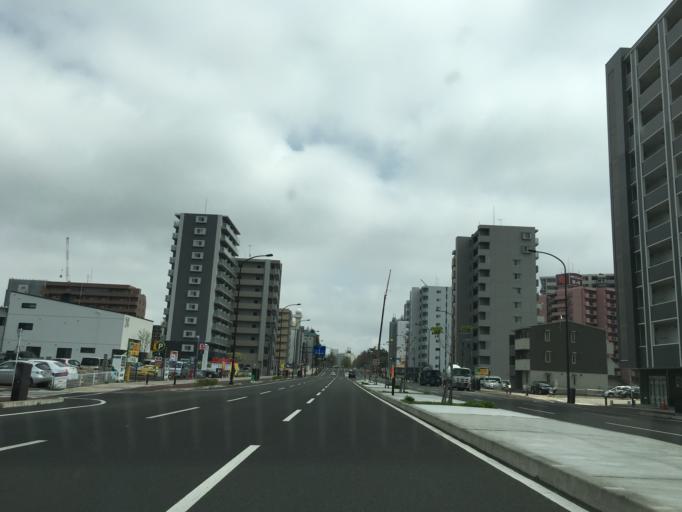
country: JP
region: Miyagi
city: Sendai-shi
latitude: 38.2625
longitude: 140.8902
